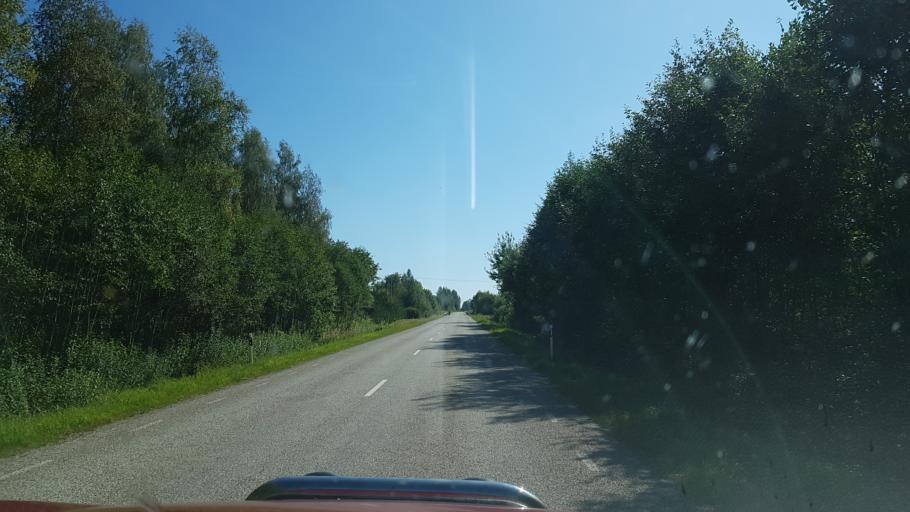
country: EE
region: Polvamaa
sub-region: Polva linn
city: Polva
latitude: 58.2448
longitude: 27.1975
